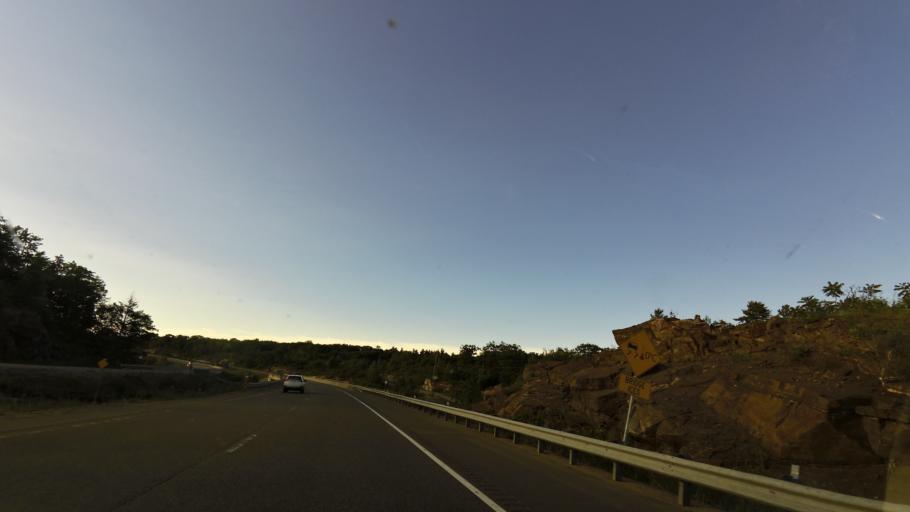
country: CA
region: Ontario
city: Midland
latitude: 44.8772
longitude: -79.7471
